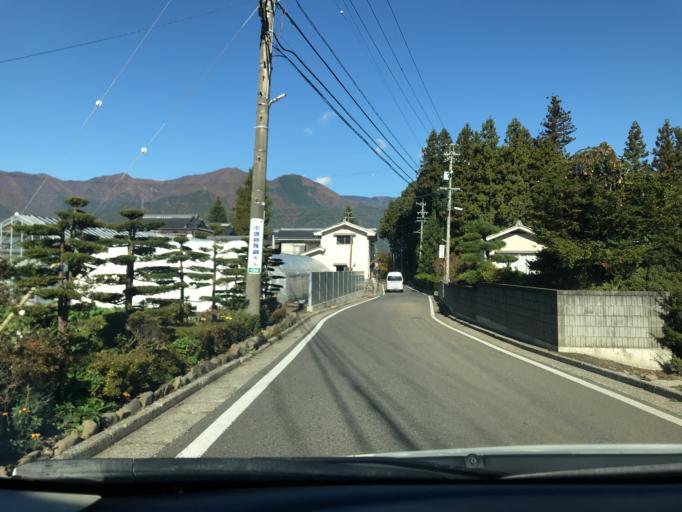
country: JP
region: Nagano
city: Matsumoto
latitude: 36.1866
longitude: 137.8564
